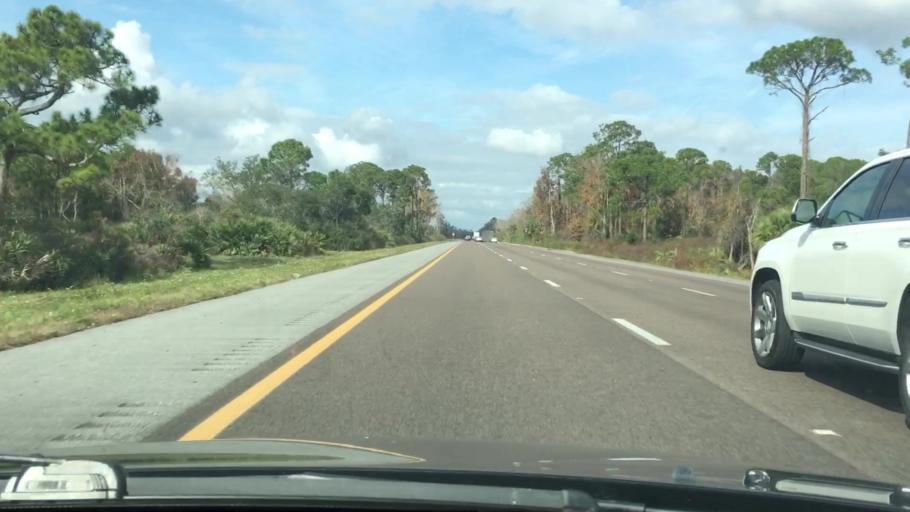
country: US
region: Florida
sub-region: Volusia County
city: Oak Hill
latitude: 28.8886
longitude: -80.9263
